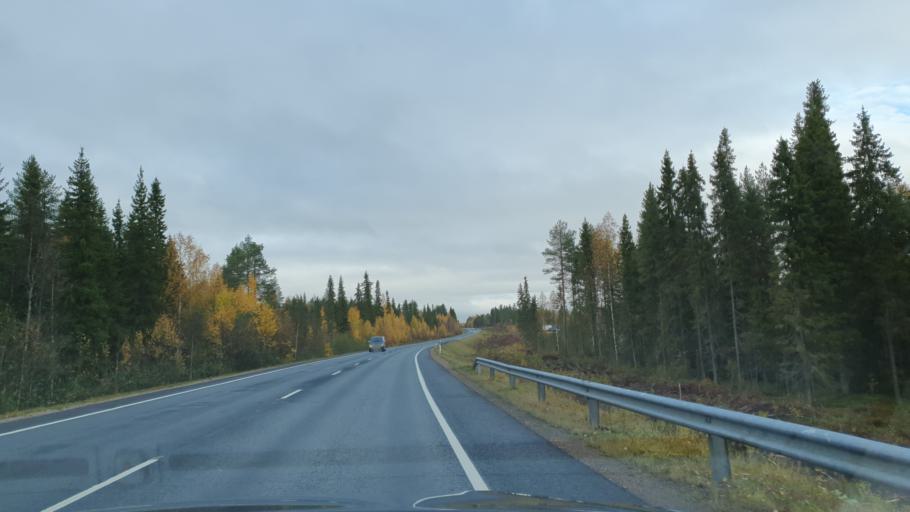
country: FI
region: Lapland
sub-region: Rovaniemi
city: Rovaniemi
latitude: 66.6159
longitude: 25.5487
